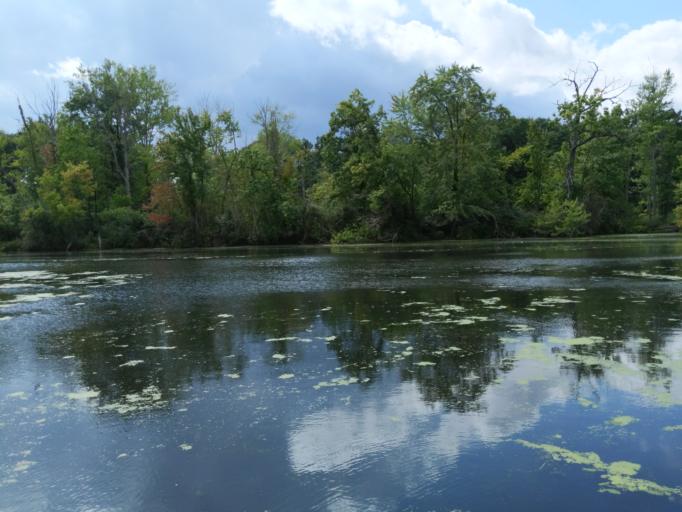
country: US
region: Michigan
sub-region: Eaton County
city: Eaton Rapids
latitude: 42.4827
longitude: -84.5819
